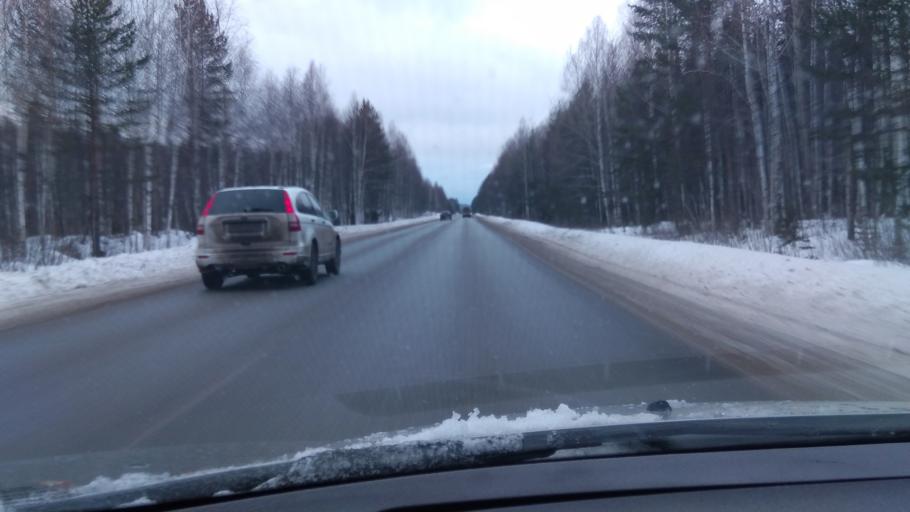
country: RU
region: Sverdlovsk
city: Iset'
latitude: 57.1115
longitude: 60.3387
